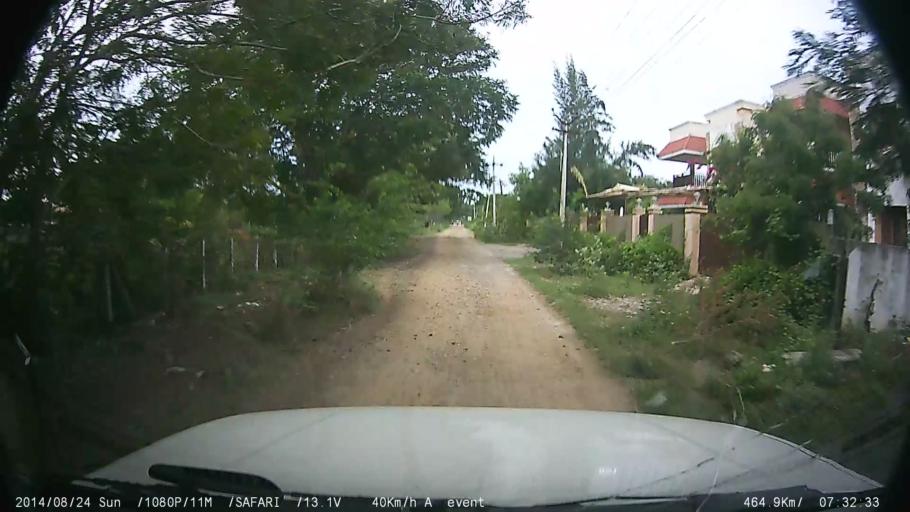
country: IN
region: Tamil Nadu
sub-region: Kancheepuram
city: Vengavasal
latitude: 12.8163
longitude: 80.2171
